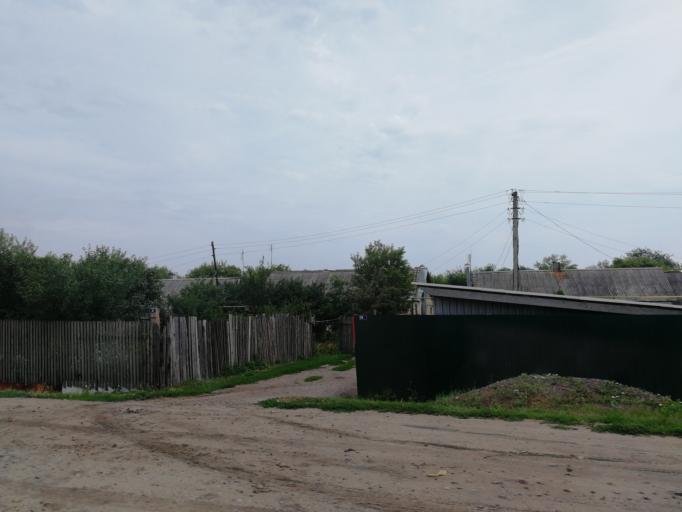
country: RU
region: Tula
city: Tovarkovskiy
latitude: 53.7009
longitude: 38.1615
